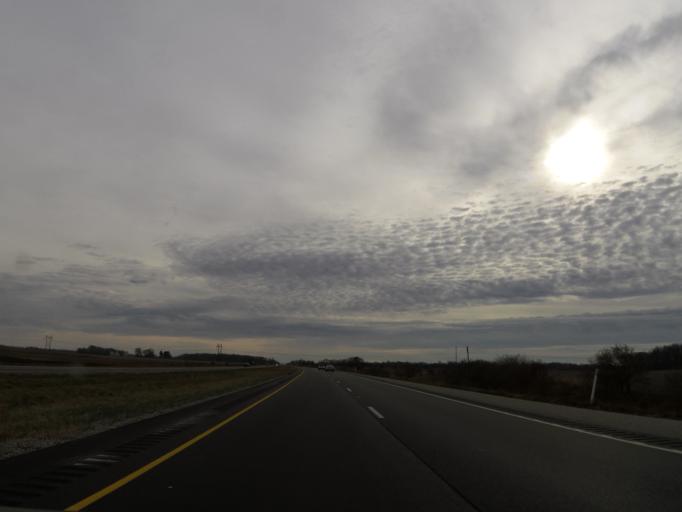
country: US
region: Indiana
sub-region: Montgomery County
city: Crawfordsville
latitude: 40.0080
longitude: -86.7532
